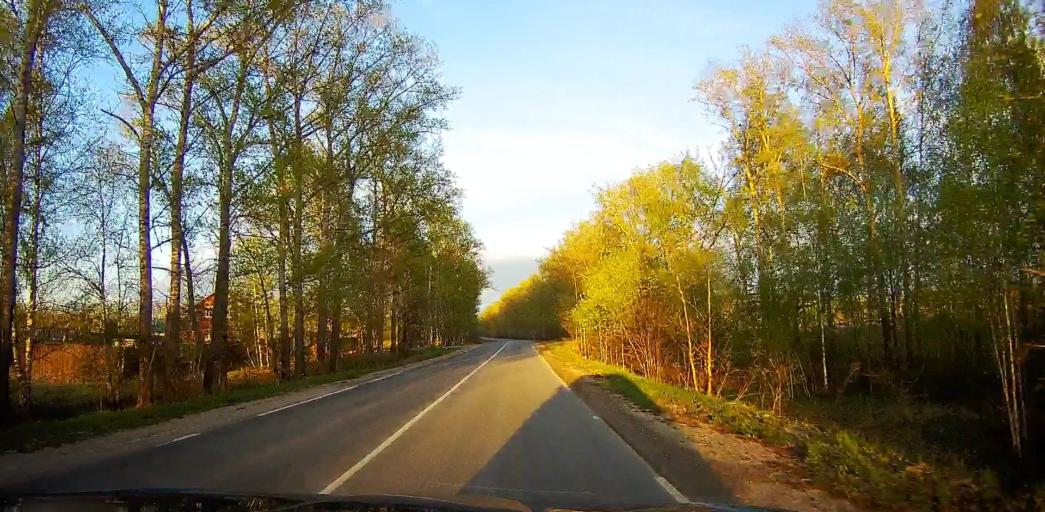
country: RU
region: Moskovskaya
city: Peski
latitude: 55.2093
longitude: 38.7135
